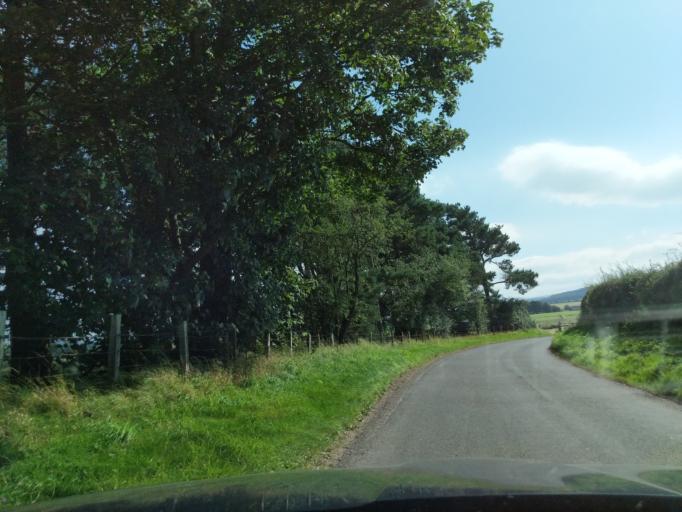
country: GB
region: England
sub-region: Northumberland
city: Ford
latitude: 55.6427
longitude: -2.1367
